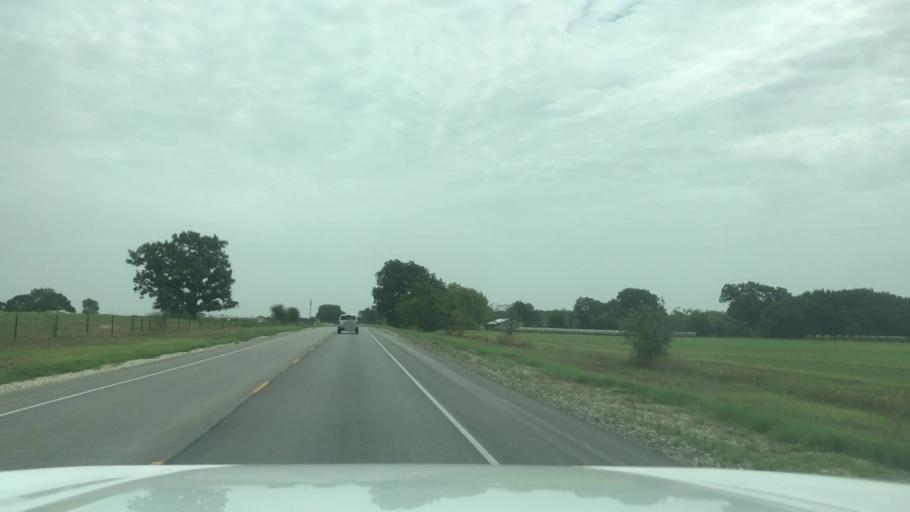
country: US
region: Texas
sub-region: Erath County
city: Dublin
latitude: 32.0902
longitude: -98.2833
